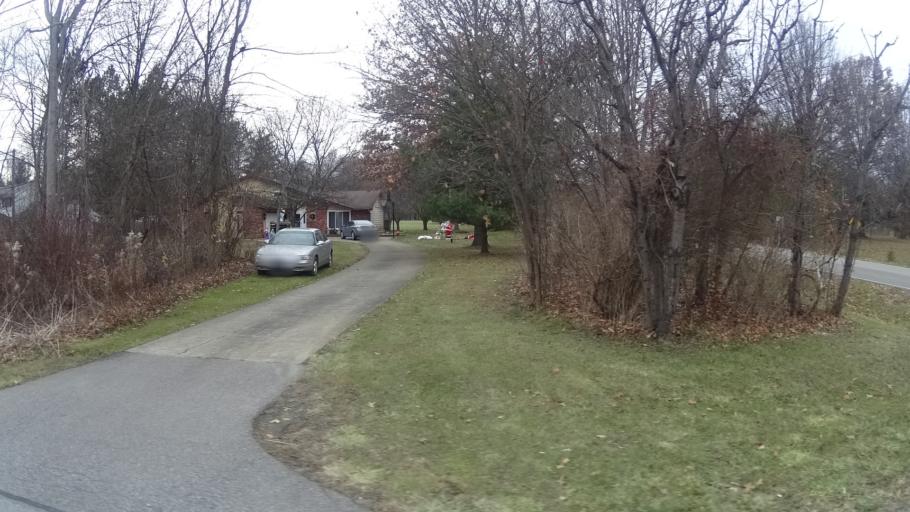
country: US
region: Ohio
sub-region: Lorain County
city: Eaton Estates
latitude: 41.2921
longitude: -81.9541
